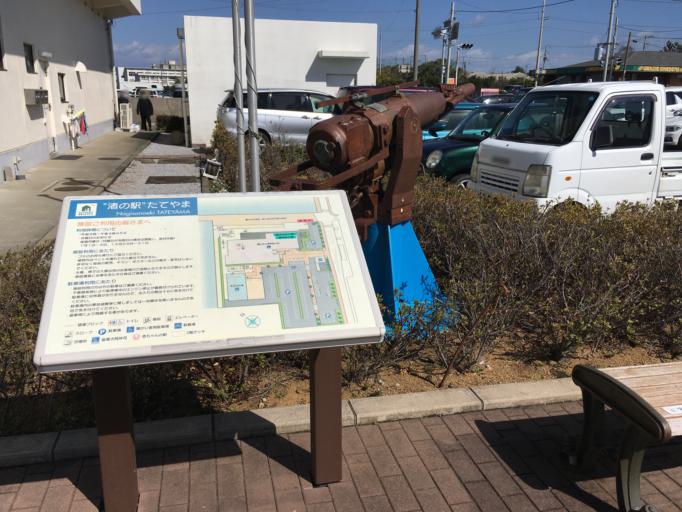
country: JP
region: Chiba
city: Tateyama
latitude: 34.9895
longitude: 139.8550
